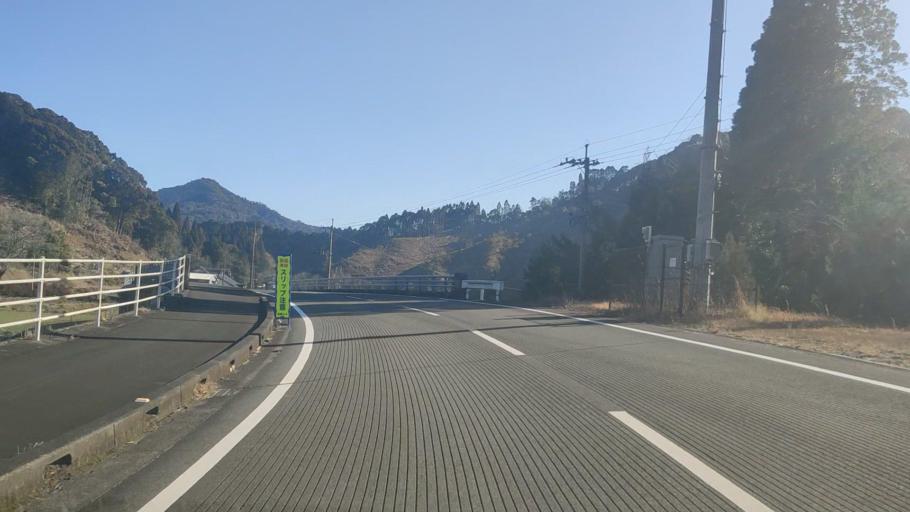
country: JP
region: Oita
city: Saiki
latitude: 32.7731
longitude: 131.8165
